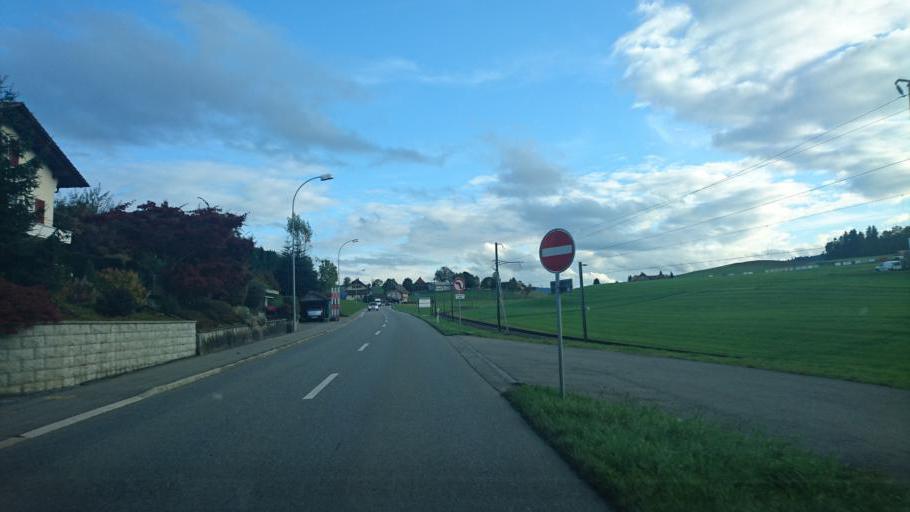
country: CH
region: Bern
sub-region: Bern-Mittelland District
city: Biglen
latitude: 46.9239
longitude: 7.6309
